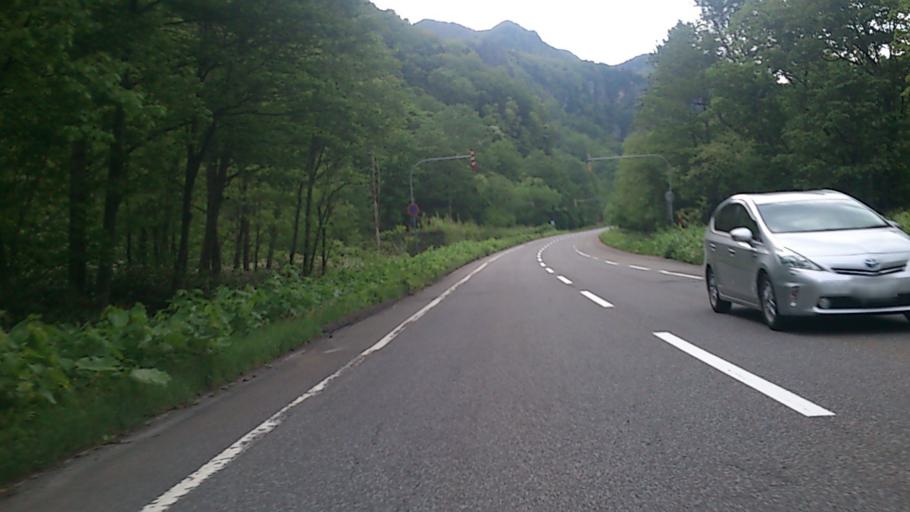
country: JP
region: Hokkaido
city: Kamikawa
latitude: 43.7571
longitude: 142.9242
